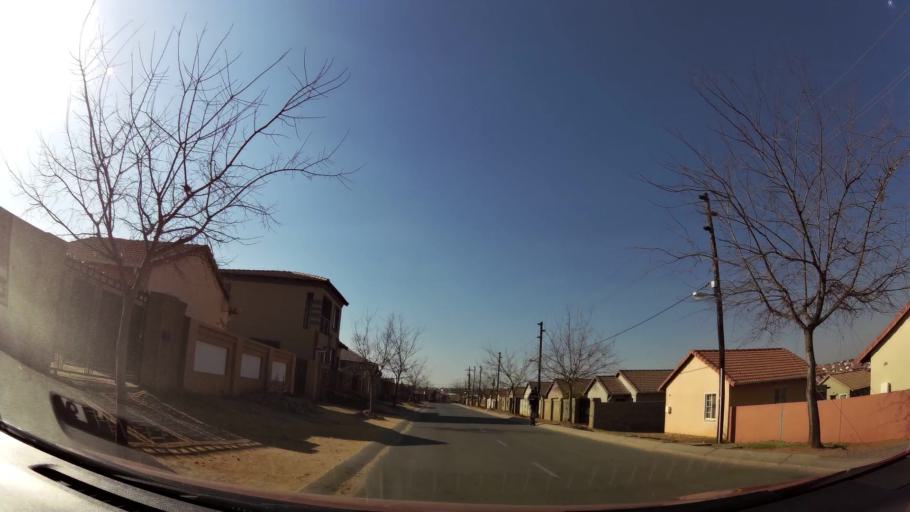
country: ZA
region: Gauteng
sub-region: West Rand District Municipality
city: Muldersdriseloop
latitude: -26.0349
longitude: 27.9179
